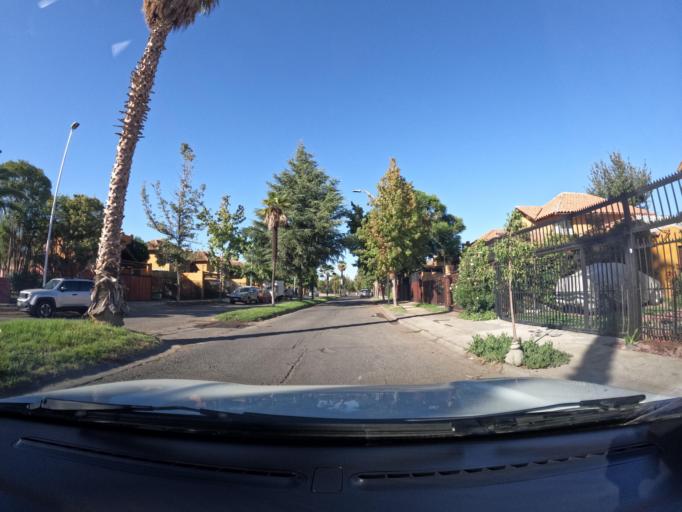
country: CL
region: Santiago Metropolitan
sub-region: Provincia de Santiago
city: Villa Presidente Frei, Nunoa, Santiago, Chile
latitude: -33.4818
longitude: -70.5508
